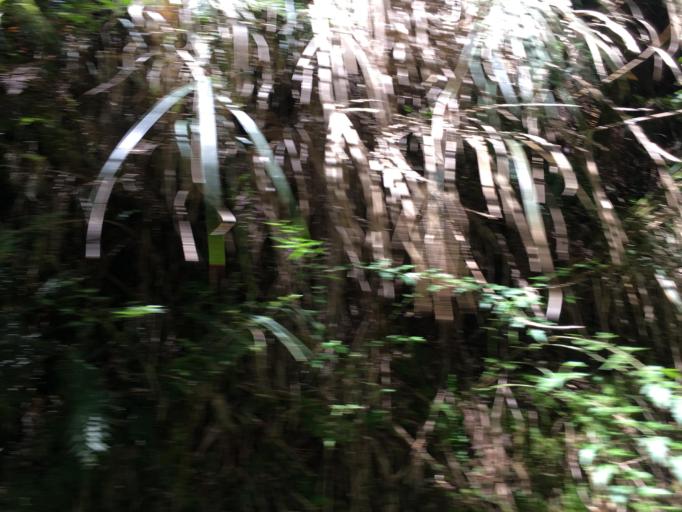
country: TW
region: Taiwan
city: Daxi
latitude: 24.5502
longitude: 121.3989
